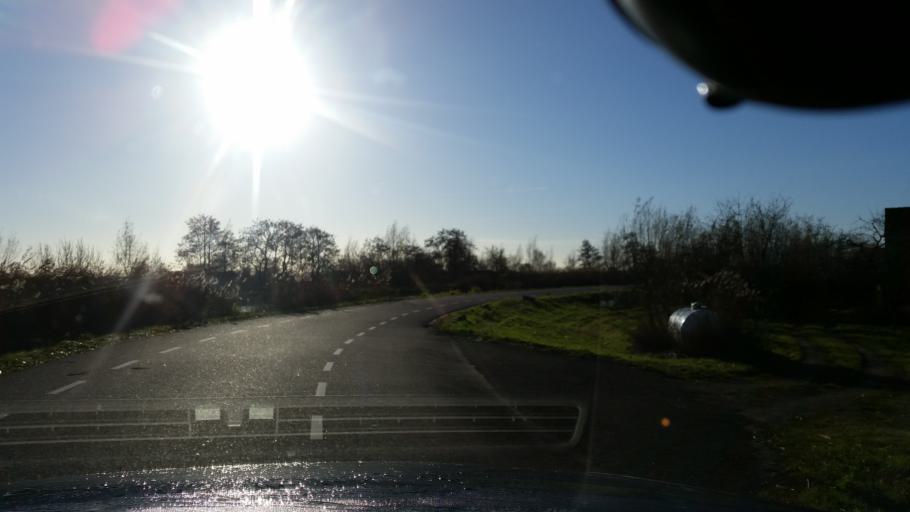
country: NL
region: North Holland
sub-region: Gemeente Ouder-Amstel
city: Ouderkerk aan de Amstel
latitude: 52.2741
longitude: 4.9274
